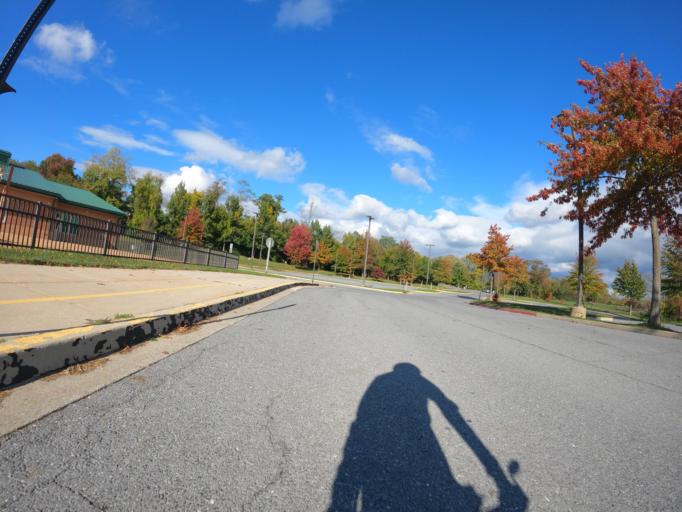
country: US
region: Maryland
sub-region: Carroll County
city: Mount Airy
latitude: 39.3787
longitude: -77.1465
